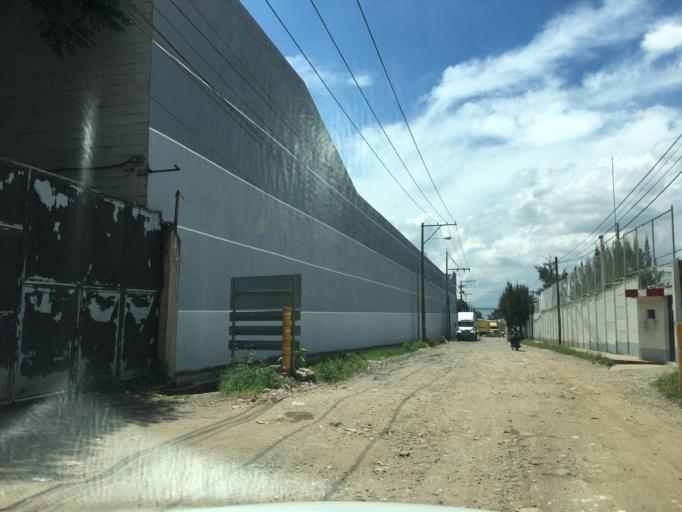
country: GT
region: Guatemala
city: Santa Catarina Pinula
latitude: 14.5901
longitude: -90.5395
